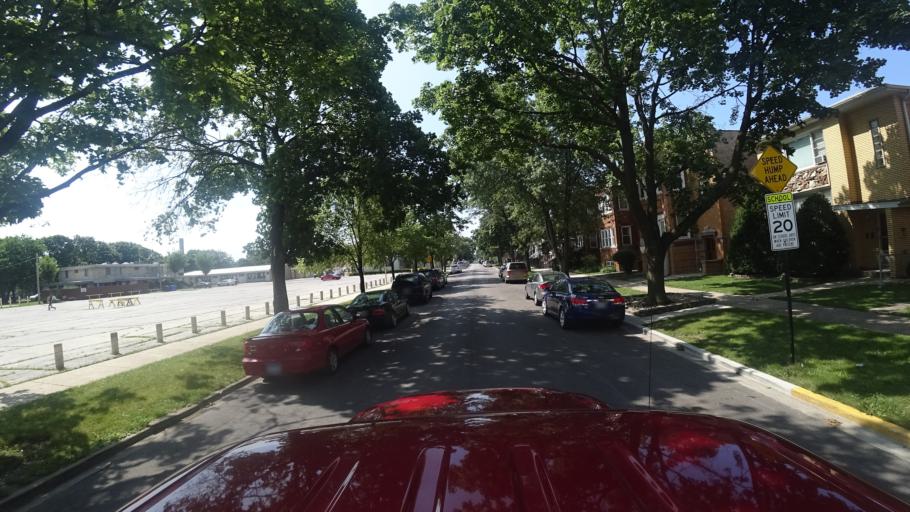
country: US
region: Illinois
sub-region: Cook County
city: Chicago
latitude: 41.7955
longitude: -87.6915
